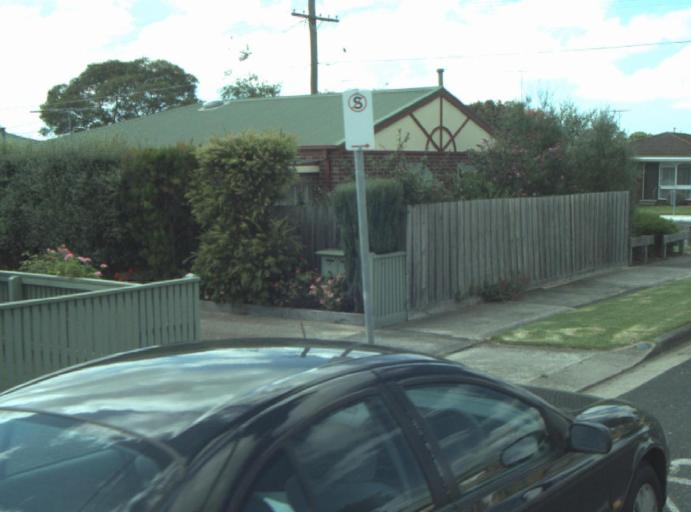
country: AU
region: Victoria
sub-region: Greater Geelong
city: Breakwater
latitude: -38.1748
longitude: 144.3491
